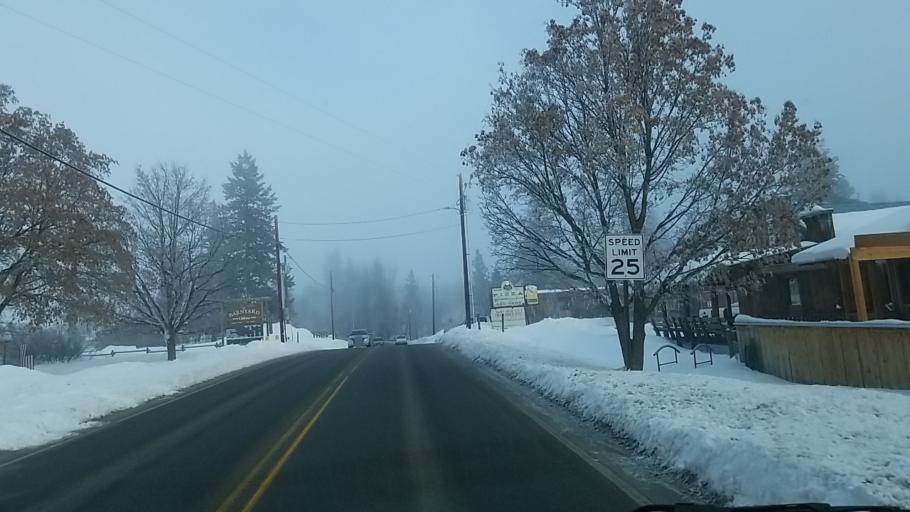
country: US
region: Washington
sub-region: Okanogan County
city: Brewster
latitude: 48.4687
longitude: -120.1763
